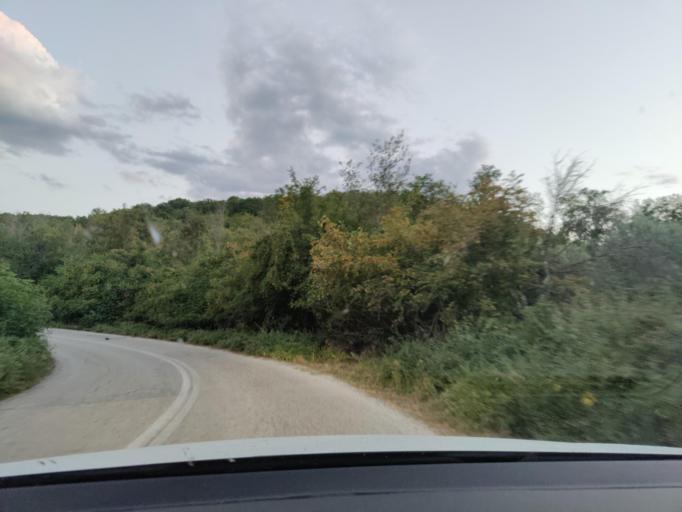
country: GR
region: Central Macedonia
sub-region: Nomos Serron
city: Chrysochorafa
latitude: 41.1577
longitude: 23.1929
